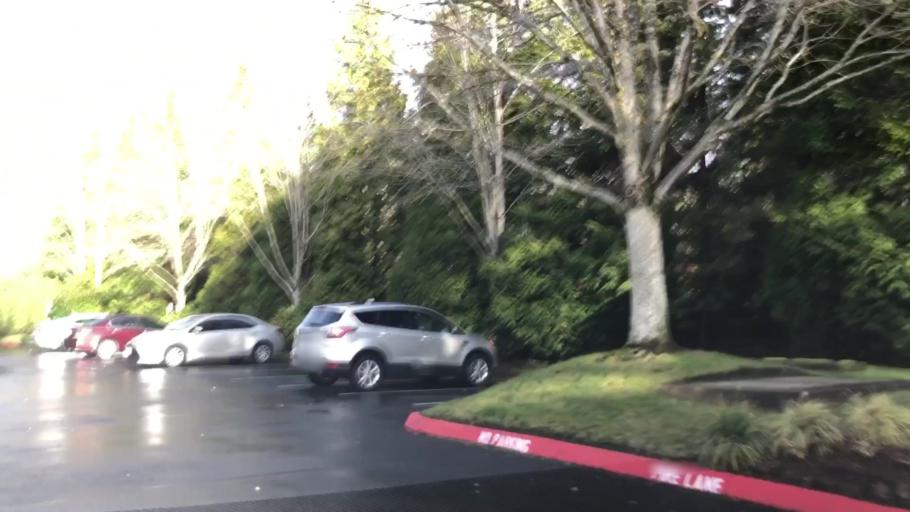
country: US
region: Washington
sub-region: King County
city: Eastgate
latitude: 47.5812
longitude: -122.1333
